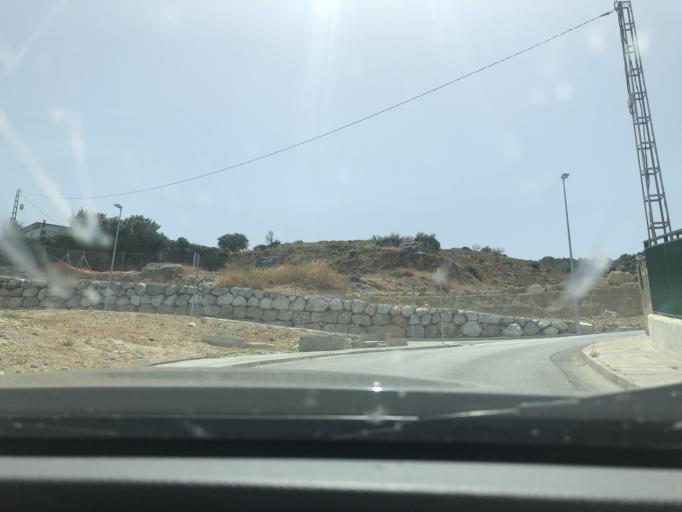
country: ES
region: Andalusia
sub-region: Provincia de Malaga
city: Cartama
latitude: 36.7130
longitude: -4.6260
